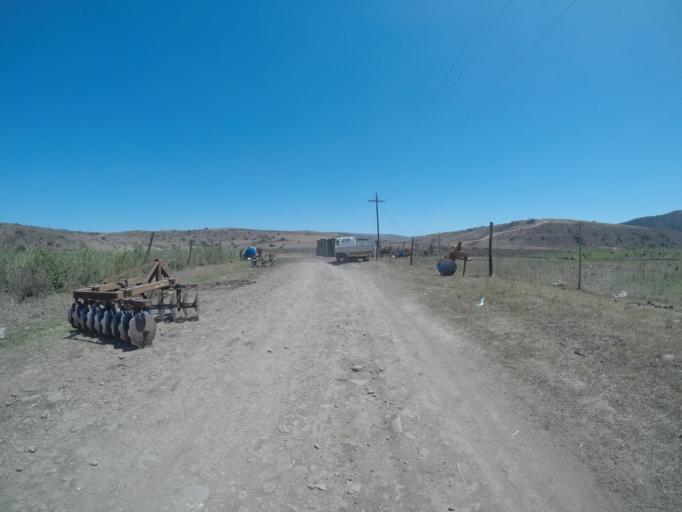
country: ZA
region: Eastern Cape
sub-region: OR Tambo District Municipality
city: Mthatha
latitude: -31.8694
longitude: 28.8710
